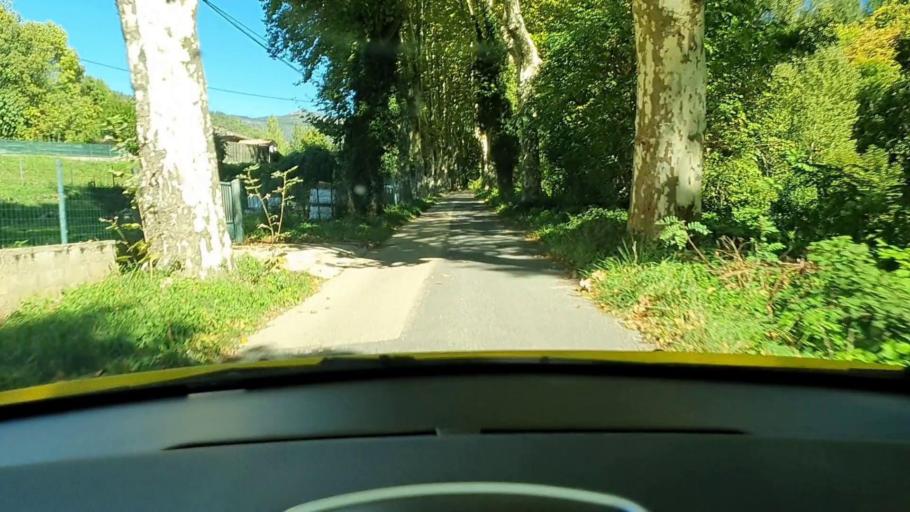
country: FR
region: Languedoc-Roussillon
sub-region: Departement du Gard
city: Le Vigan
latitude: 43.9761
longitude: 3.4421
